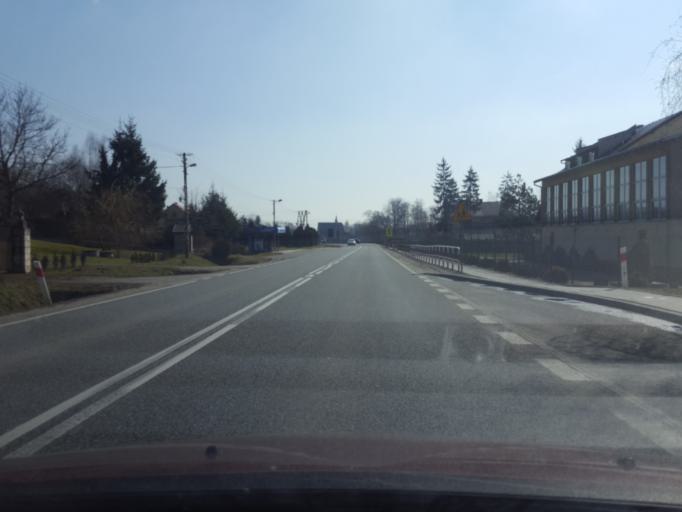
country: PL
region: Lesser Poland Voivodeship
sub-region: Powiat brzeski
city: Czchow
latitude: 49.8533
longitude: 20.6577
